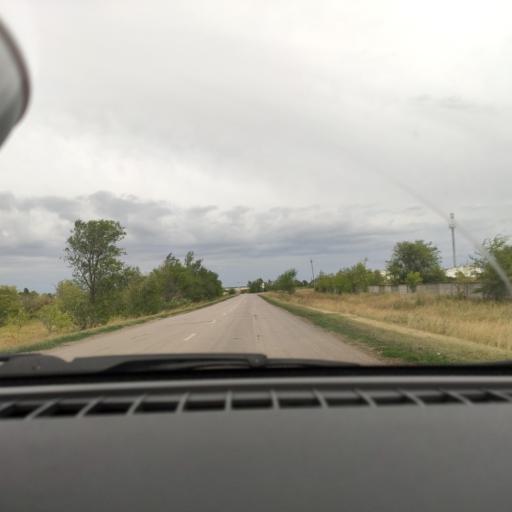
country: RU
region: Samara
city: Georgiyevka
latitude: 53.4727
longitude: 50.9375
